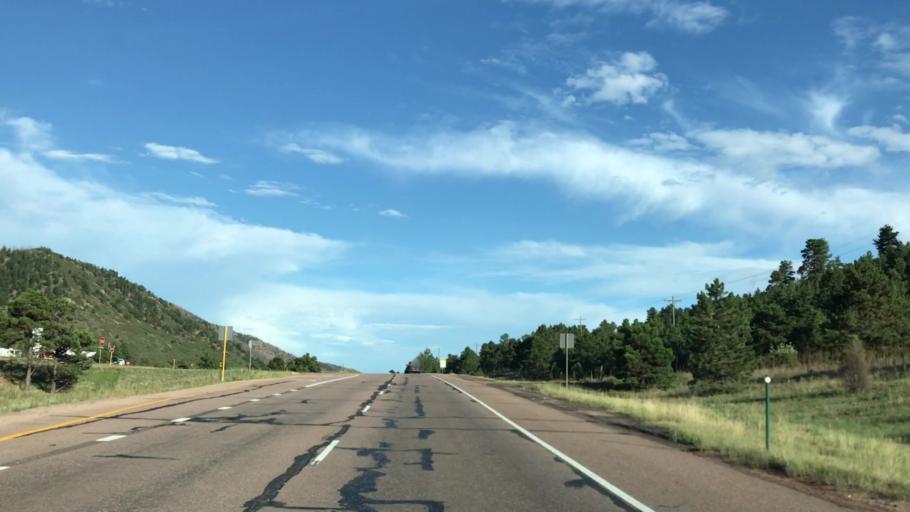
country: US
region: Colorado
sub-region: El Paso County
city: Cascade-Chipita Park
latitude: 38.9358
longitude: -105.0090
